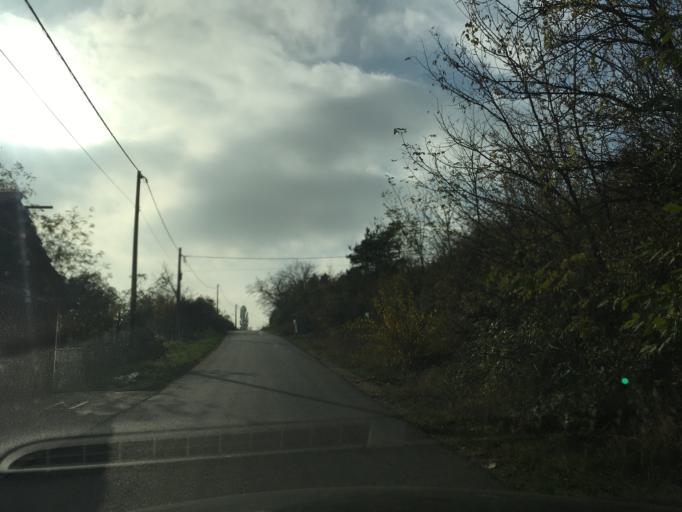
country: RS
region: Central Serbia
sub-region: Belgrade
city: Sopot
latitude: 44.4876
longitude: 20.5653
